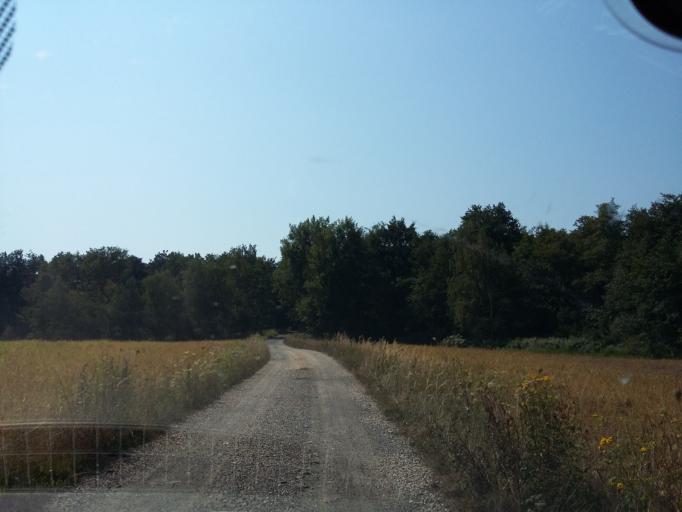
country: SI
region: Hodos-Hodos
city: Hodos
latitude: 46.8413
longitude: 16.3177
